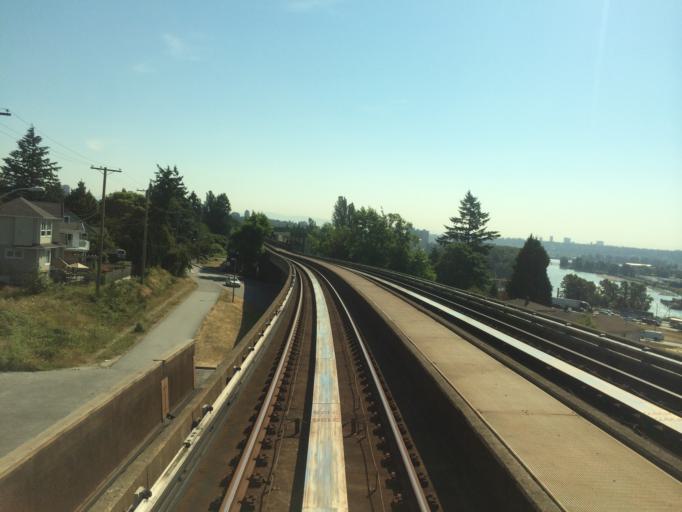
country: CA
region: British Columbia
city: New Westminster
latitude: 49.1996
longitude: -122.9511
